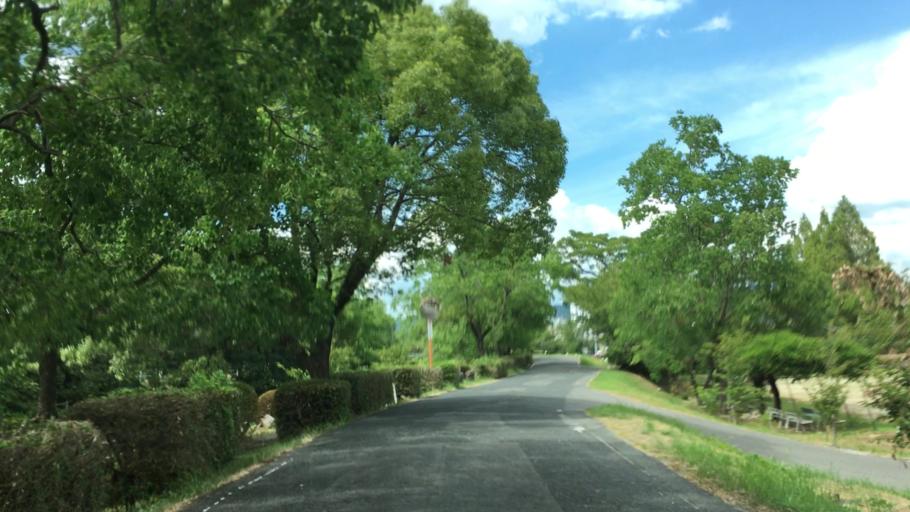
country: JP
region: Saga Prefecture
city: Saga-shi
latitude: 33.2709
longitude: 130.2825
